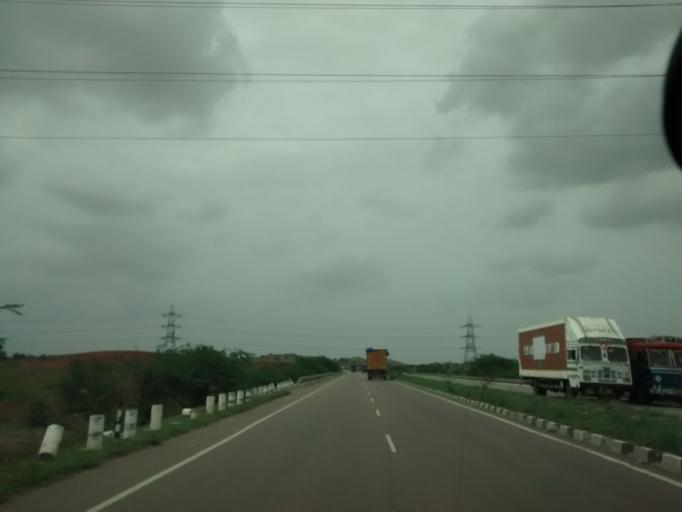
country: IN
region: Andhra Pradesh
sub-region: Kurnool
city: Ramapuram
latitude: 15.1475
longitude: 77.6654
